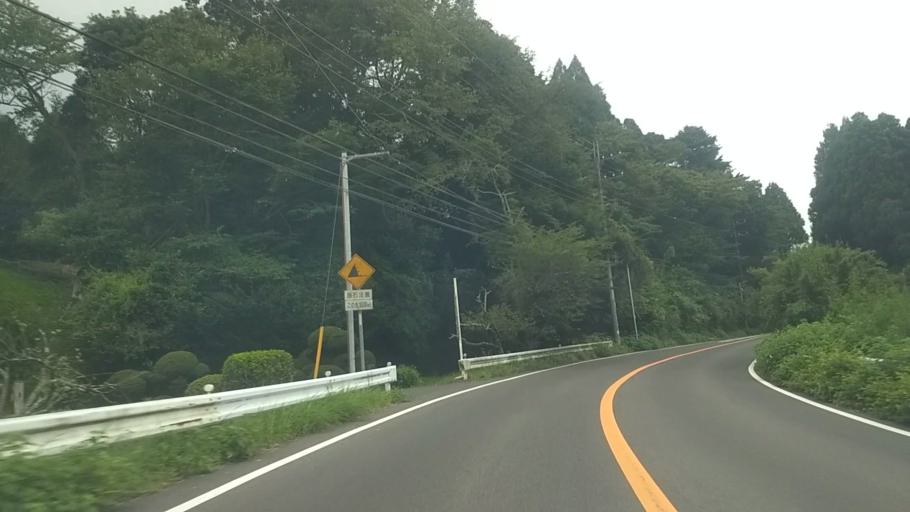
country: JP
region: Chiba
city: Kawaguchi
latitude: 35.2197
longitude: 140.0750
